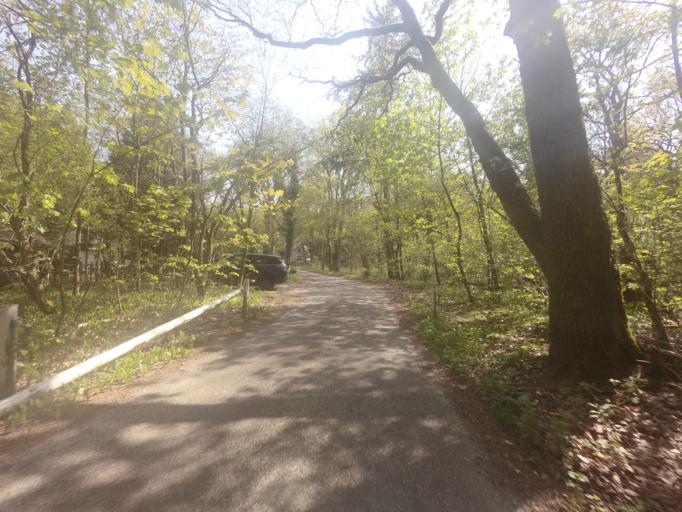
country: NL
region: North Holland
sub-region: Gemeente Hilversum
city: Hilversum
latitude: 52.1864
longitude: 5.2244
